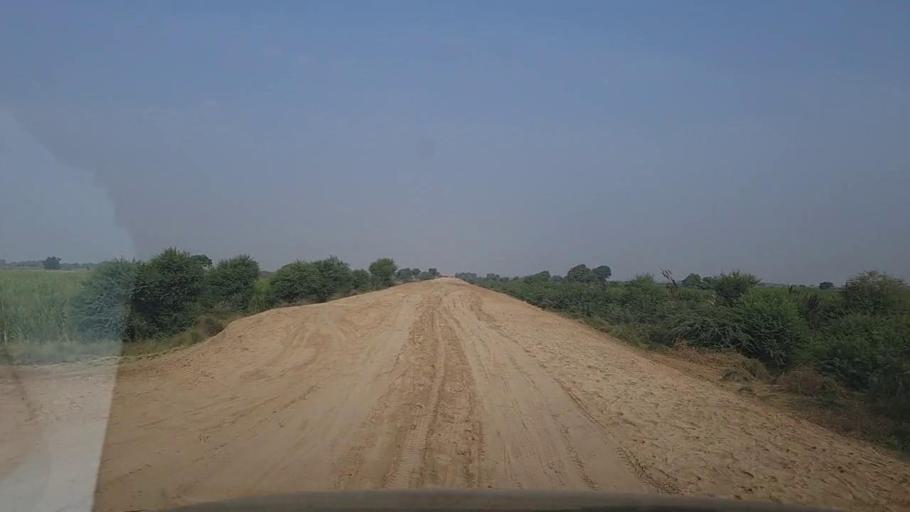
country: PK
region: Sindh
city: Bulri
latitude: 24.9879
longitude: 68.2936
